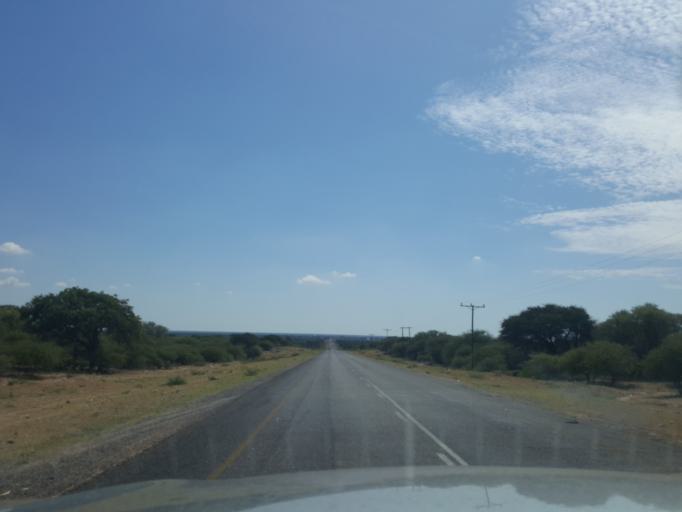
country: BW
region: Kweneng
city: Letlhakeng
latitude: -24.1214
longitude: 25.0820
